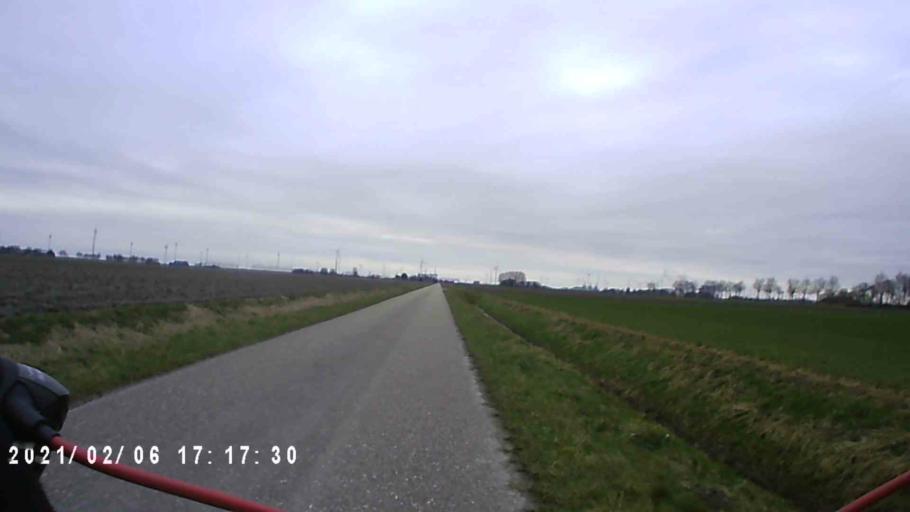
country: NL
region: Groningen
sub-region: Gemeente Appingedam
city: Appingedam
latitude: 53.4243
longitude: 6.7867
